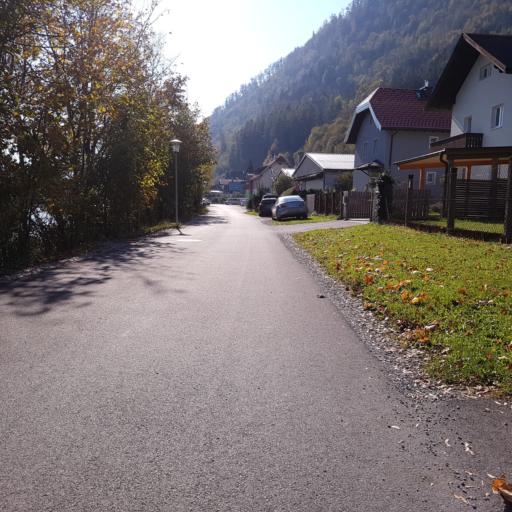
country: AT
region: Salzburg
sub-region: Politischer Bezirk Hallein
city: Oberalm
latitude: 47.6927
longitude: 13.0825
